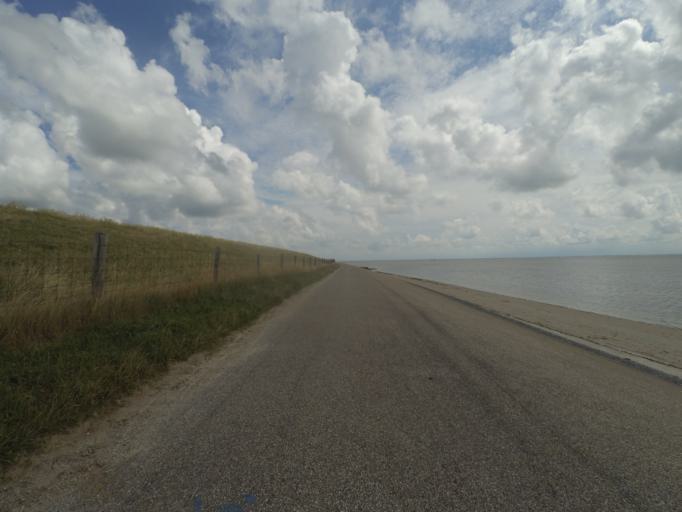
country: NL
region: North Holland
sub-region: Gemeente Texel
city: Den Burg
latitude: 53.0299
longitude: 4.8271
